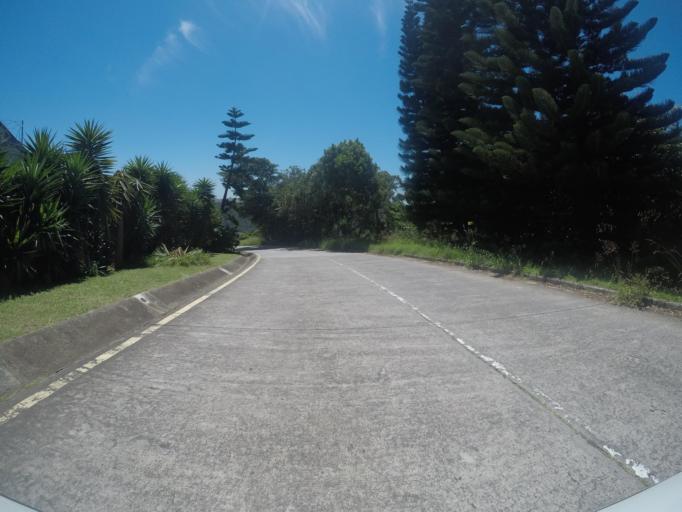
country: ZA
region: Eastern Cape
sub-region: Buffalo City Metropolitan Municipality
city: East London
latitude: -32.9325
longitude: 27.9938
